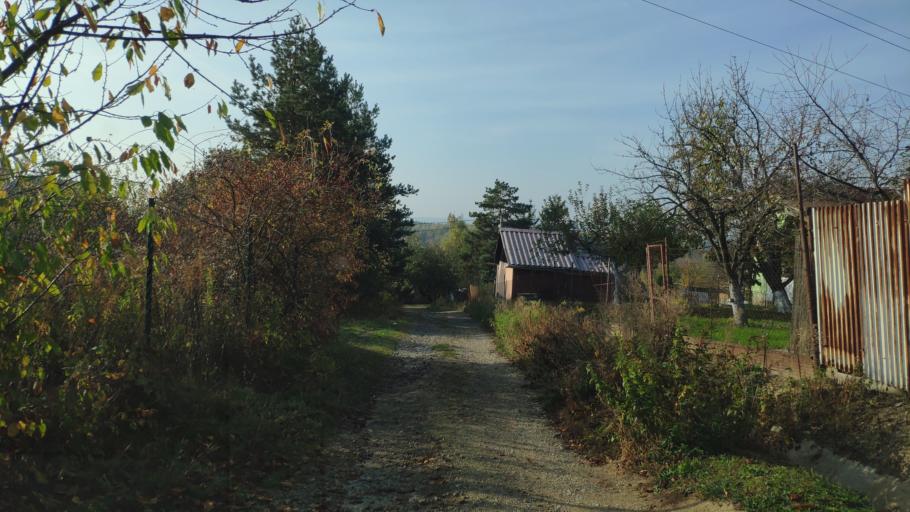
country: SK
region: Kosicky
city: Kosice
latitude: 48.7427
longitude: 21.2194
